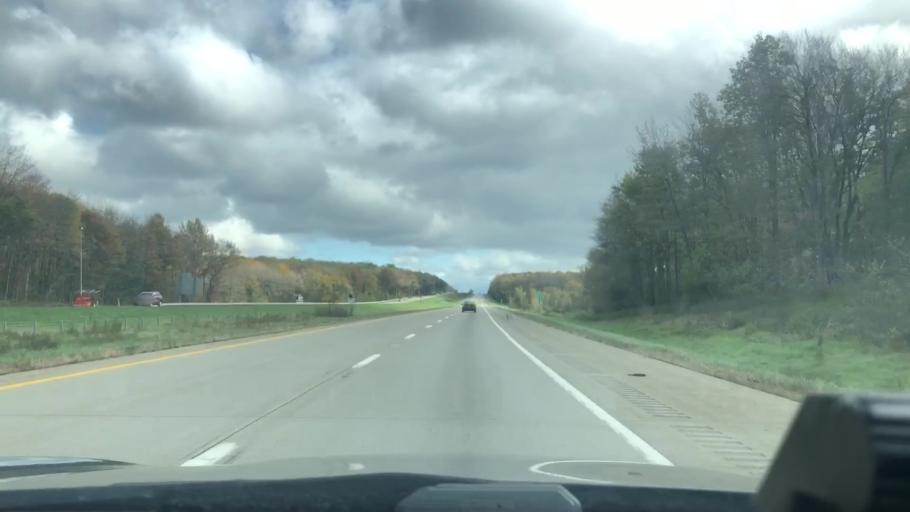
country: US
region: Pennsylvania
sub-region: Monroe County
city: Pocono Pines
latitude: 41.2206
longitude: -75.4823
